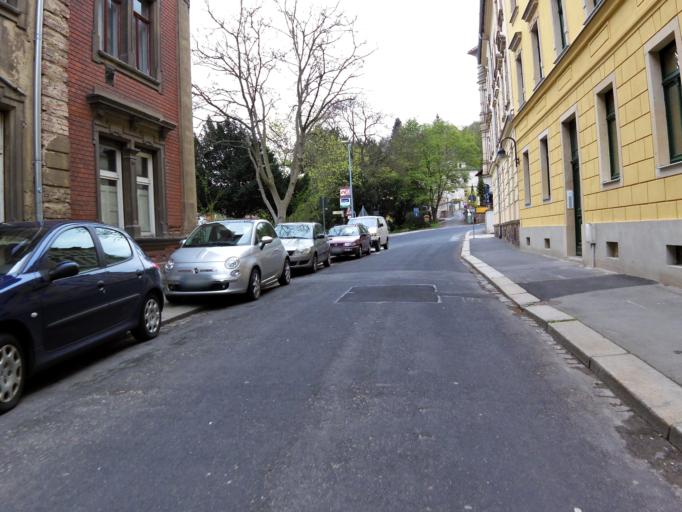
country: DE
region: Saxony
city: Meissen
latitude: 51.1575
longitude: 13.4657
